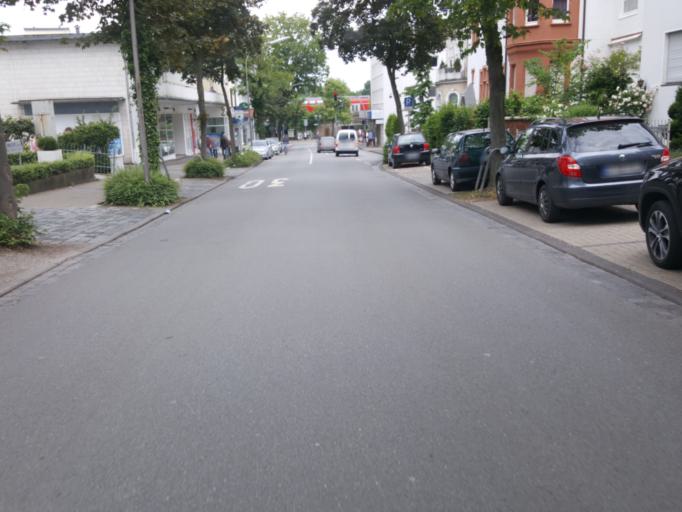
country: DE
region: North Rhine-Westphalia
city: Bad Oeynhausen
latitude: 52.2042
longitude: 8.7989
